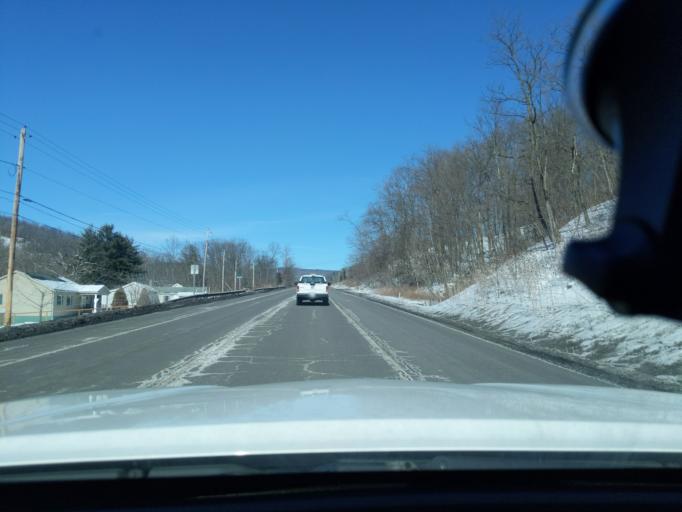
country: US
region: Maryland
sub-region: Allegany County
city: Westernport
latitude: 39.5157
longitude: -79.0202
